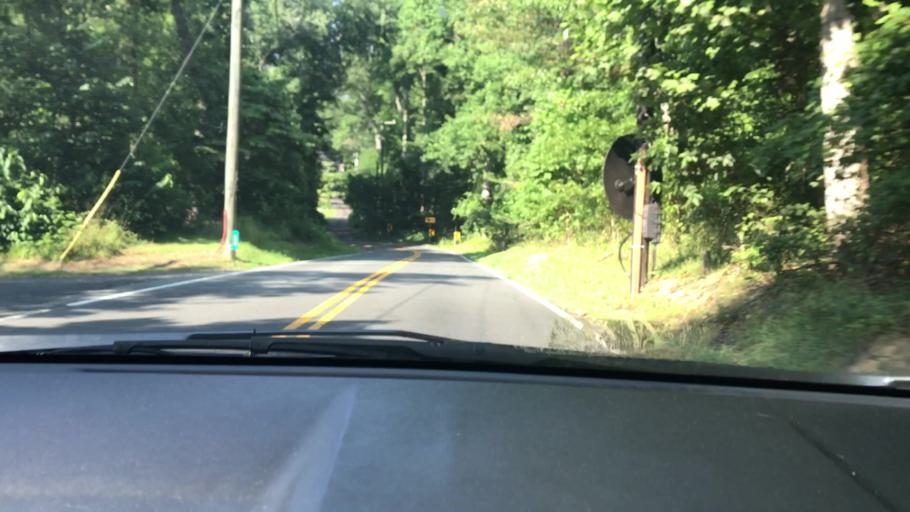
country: US
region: Virginia
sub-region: Fairfax County
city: Great Falls
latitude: 38.9869
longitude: -77.2600
